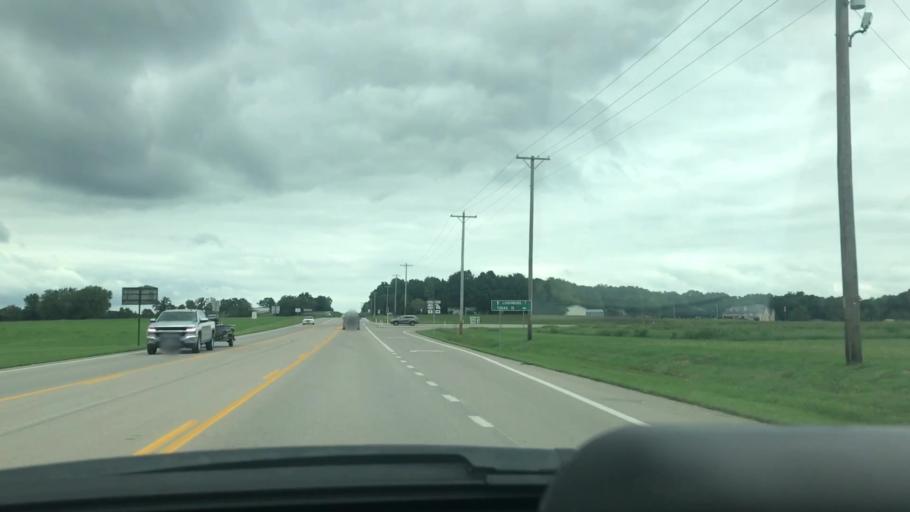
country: US
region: Missouri
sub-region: Dallas County
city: Buffalo
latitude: 37.6664
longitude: -93.1034
